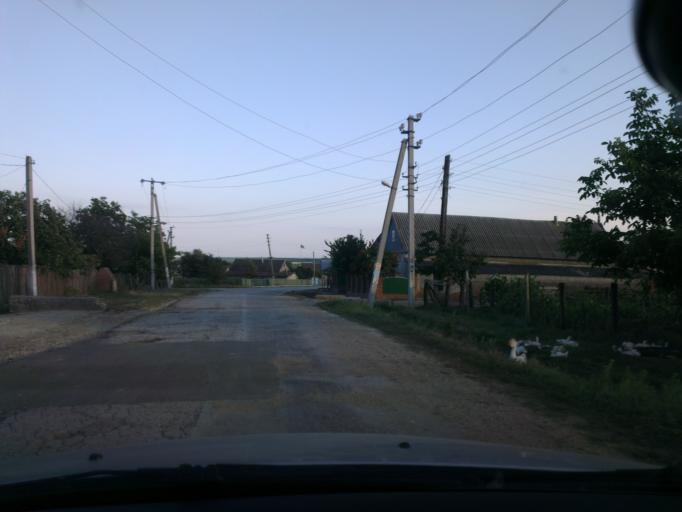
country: MD
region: Cantemir
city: Visniovca
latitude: 46.3349
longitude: 28.4020
